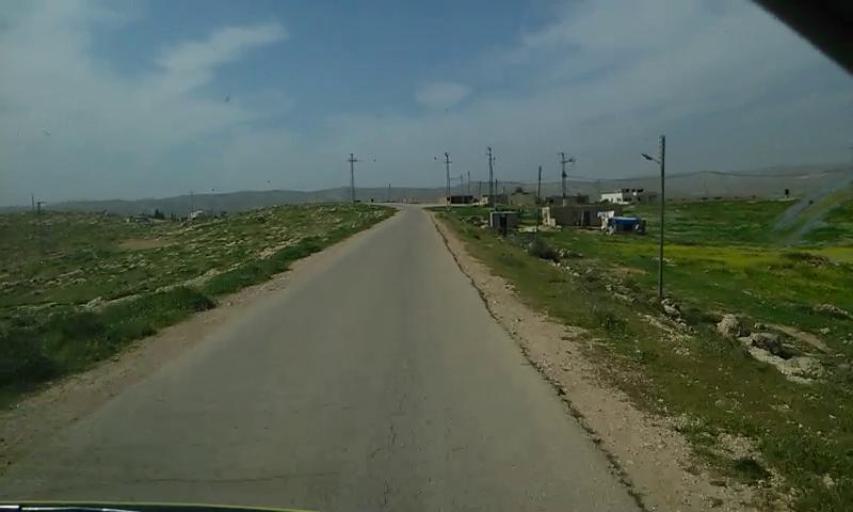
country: PS
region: West Bank
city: Khallat al Mayyah
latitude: 31.4413
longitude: 35.1991
